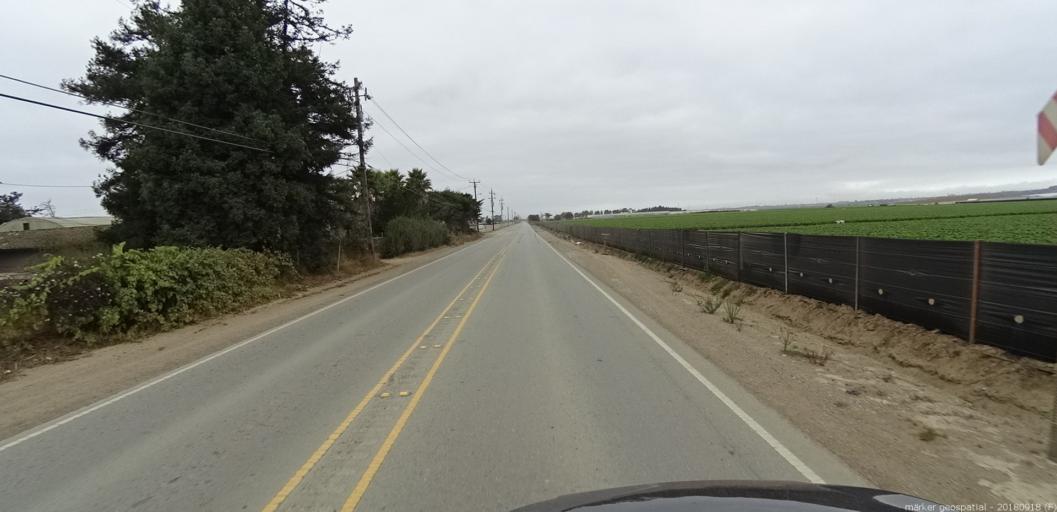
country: US
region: California
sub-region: Monterey County
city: Prunedale
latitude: 36.7399
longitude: -121.6757
